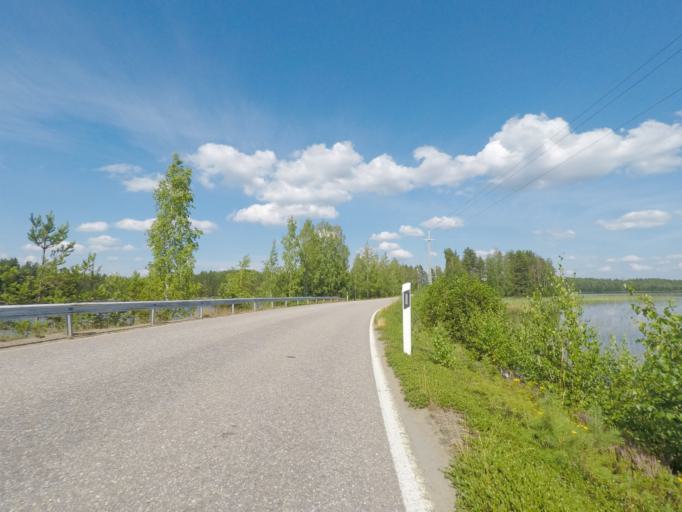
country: FI
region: Southern Savonia
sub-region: Mikkeli
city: Puumala
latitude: 61.4718
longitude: 28.1671
